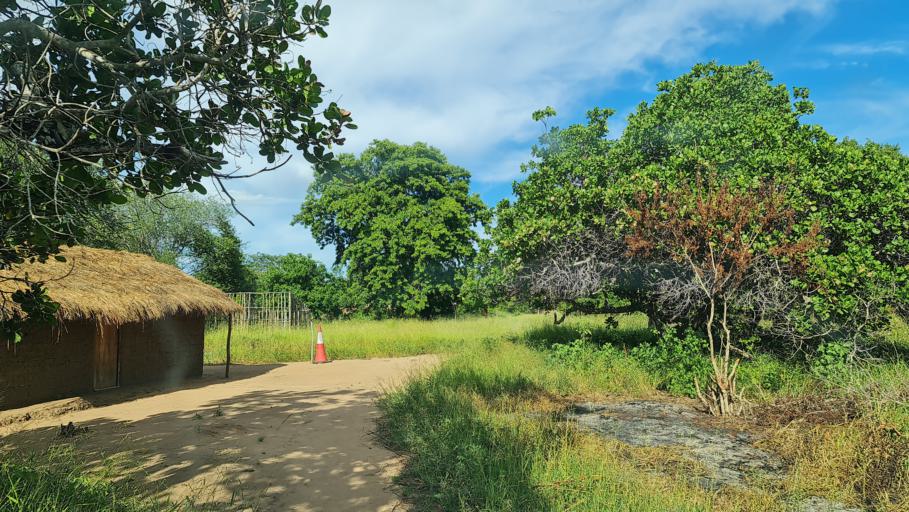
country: MZ
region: Nampula
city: Ilha de Mocambique
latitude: -15.5048
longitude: 40.1529
